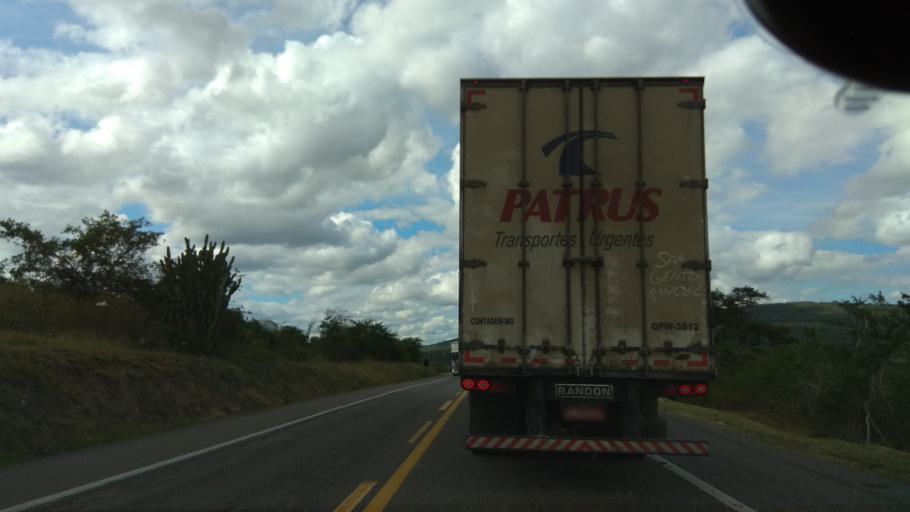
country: BR
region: Bahia
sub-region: Santa Ines
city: Santa Ines
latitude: -12.9914
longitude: -39.9482
